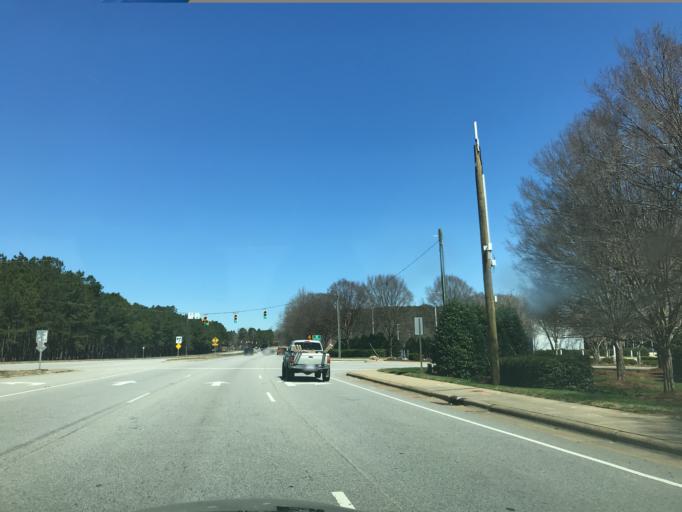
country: US
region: North Carolina
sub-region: Wake County
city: Garner
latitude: 35.7276
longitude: -78.6404
